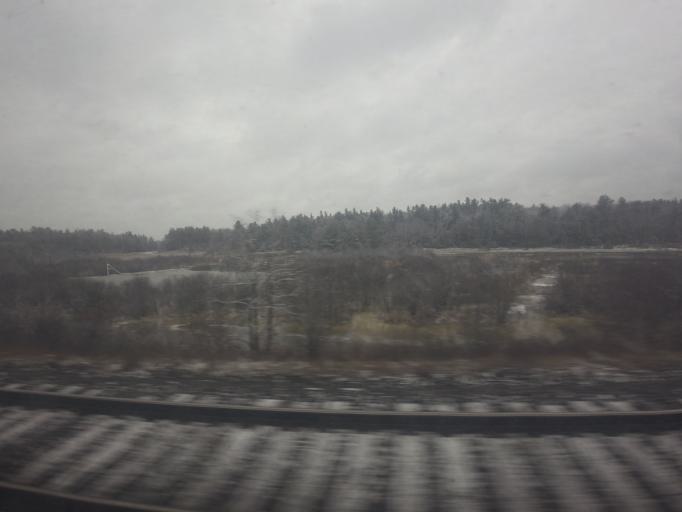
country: US
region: New York
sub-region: Jefferson County
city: Alexandria Bay
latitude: 44.4385
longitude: -75.9604
